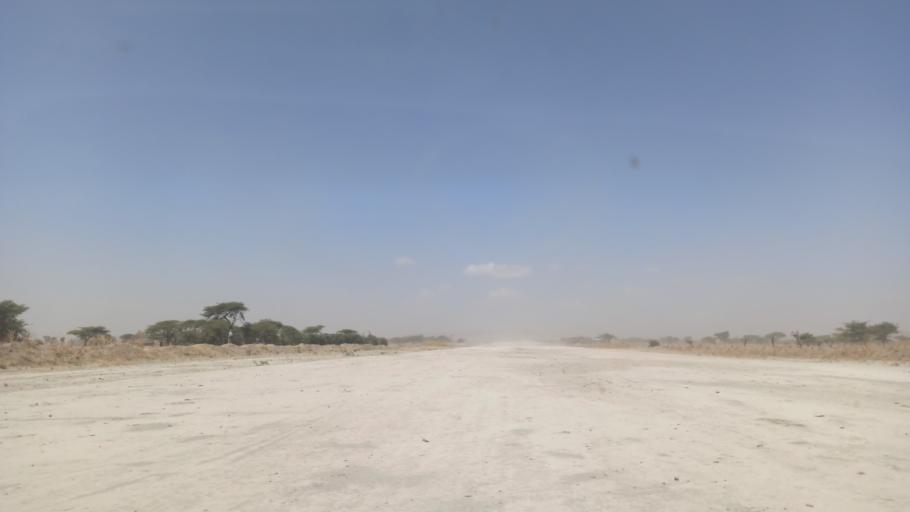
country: ET
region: Oromiya
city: Ziway
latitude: 7.7155
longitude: 38.6336
